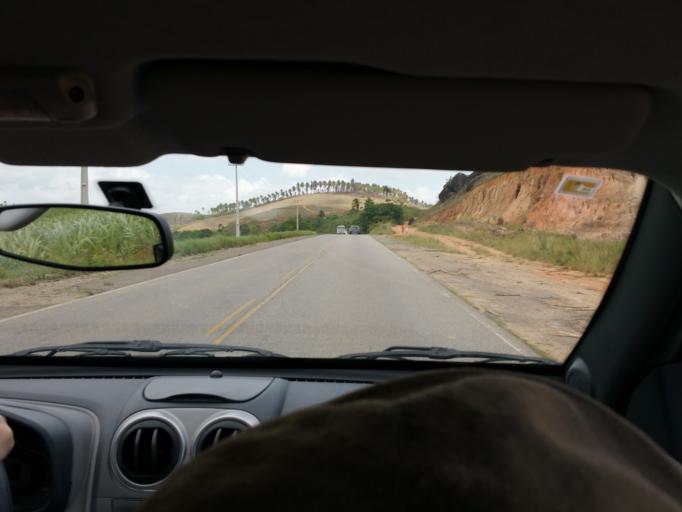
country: BR
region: Pernambuco
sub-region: Sirinhaem
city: Sirinhaem
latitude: -8.6350
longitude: -35.1188
